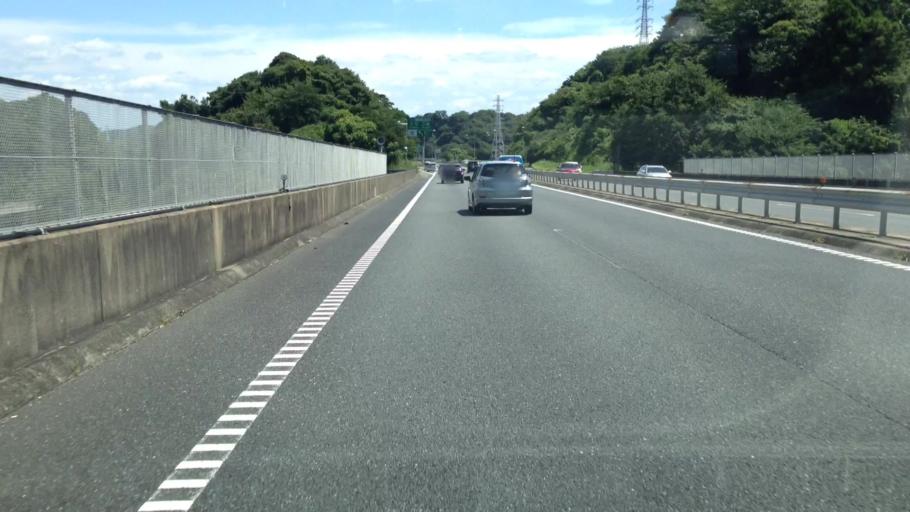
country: JP
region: Kanagawa
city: Yokosuka
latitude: 35.2433
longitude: 139.6549
